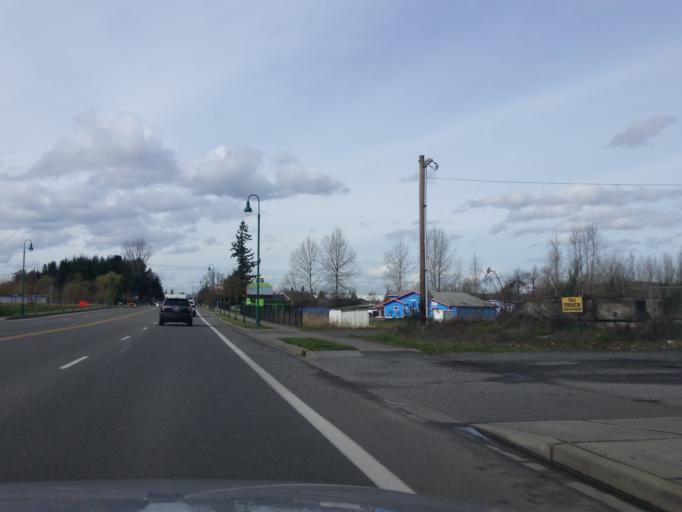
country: US
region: Washington
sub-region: Pierce County
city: Milton
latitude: 47.2247
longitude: -122.3284
